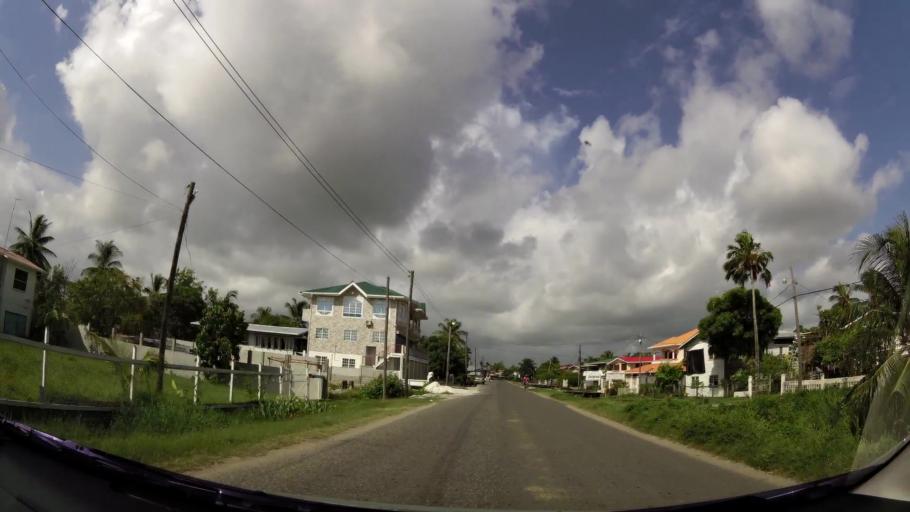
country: GY
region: Demerara-Mahaica
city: Mahaica Village
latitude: 6.6746
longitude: -57.9201
